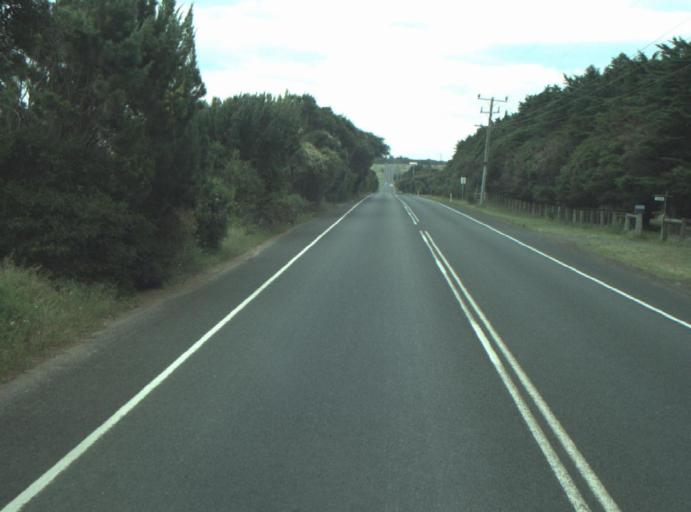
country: AU
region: Victoria
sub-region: Queenscliffe
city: Queenscliff
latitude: -38.2663
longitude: 144.5762
